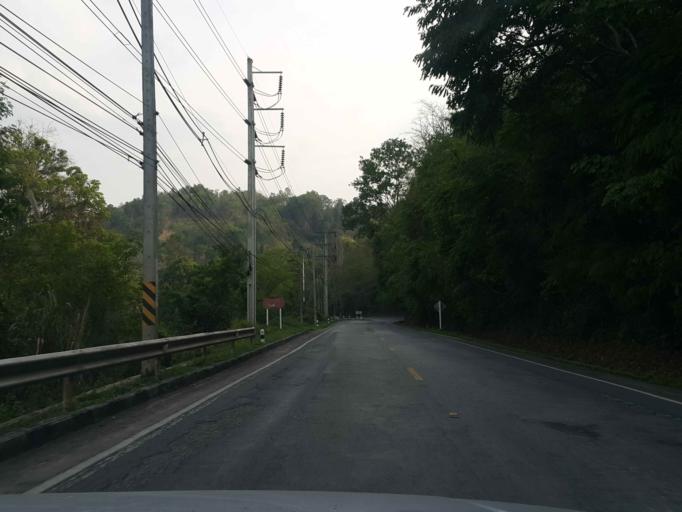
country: TH
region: Chiang Mai
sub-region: Amphoe Chiang Dao
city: Chiang Dao
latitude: 19.2661
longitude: 98.9693
